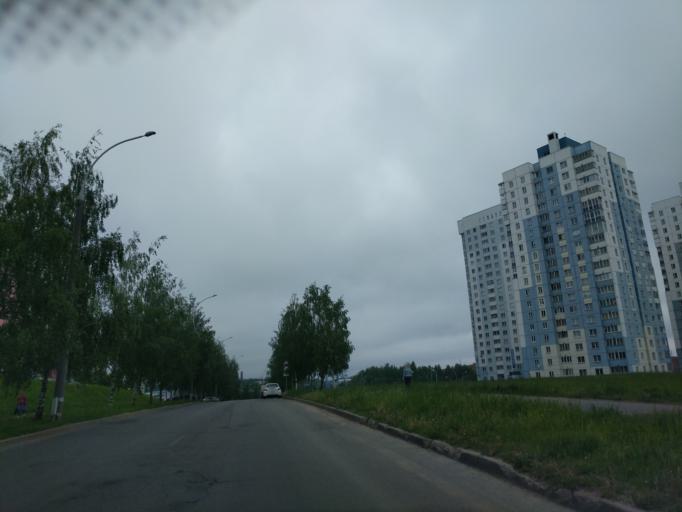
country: BY
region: Minsk
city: Novoye Medvezhino
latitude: 53.8796
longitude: 27.4516
